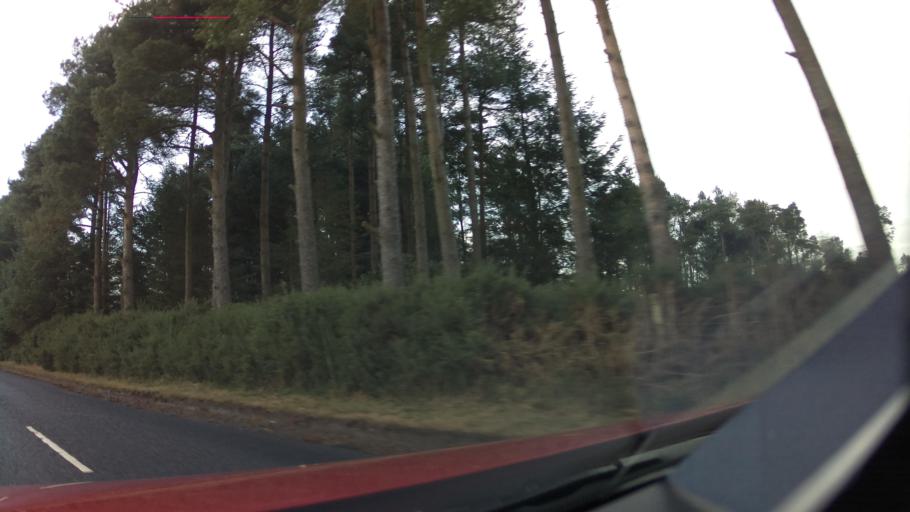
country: GB
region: Scotland
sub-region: Angus
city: Letham
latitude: 56.5560
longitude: -2.7642
